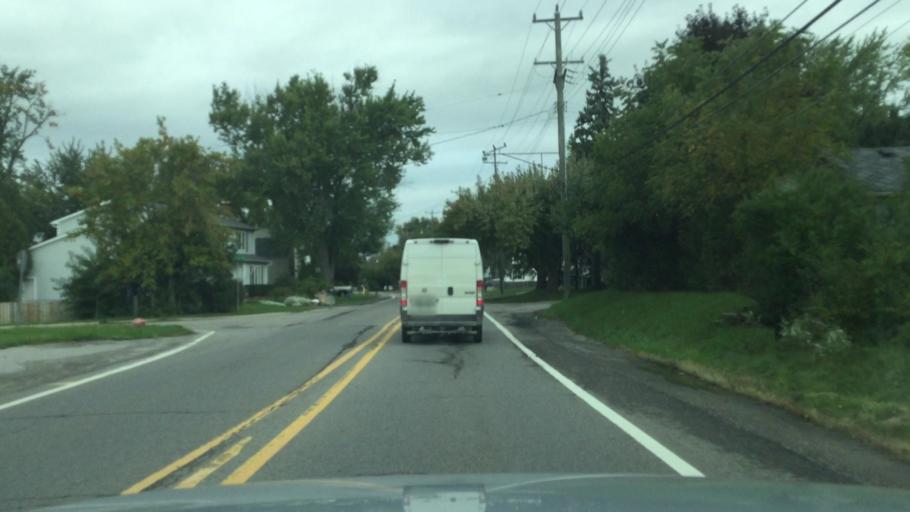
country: US
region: Michigan
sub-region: Oakland County
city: Keego Harbor
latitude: 42.6187
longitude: -83.3511
